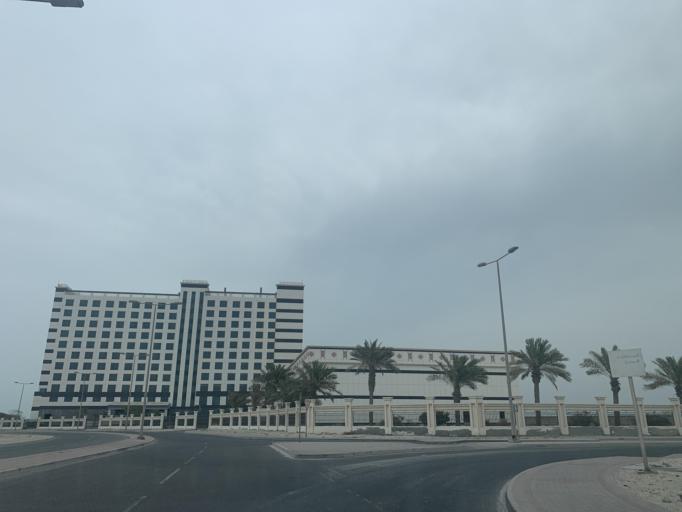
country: BH
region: Muharraq
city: Al Hadd
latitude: 26.2104
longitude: 50.6820
